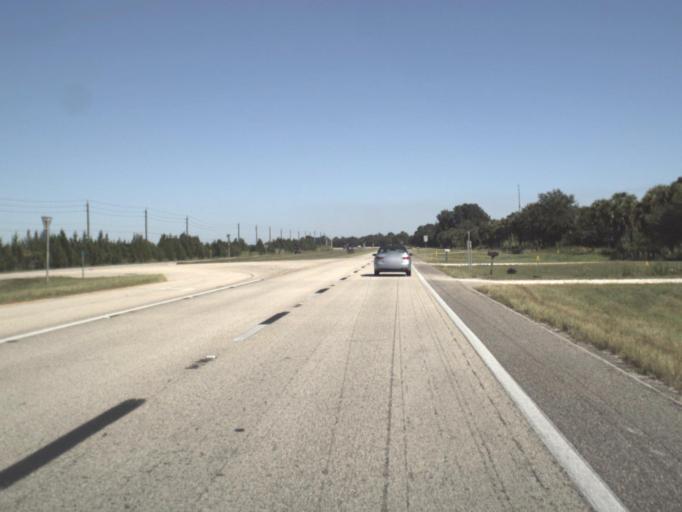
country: US
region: Florida
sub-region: Lee County
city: Alva
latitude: 26.7098
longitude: -81.5186
